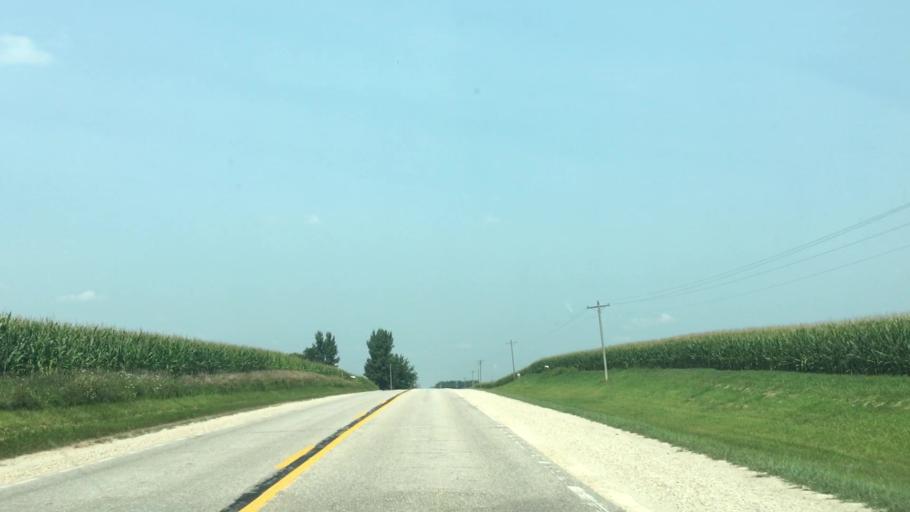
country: US
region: Iowa
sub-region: Buchanan County
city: Independence
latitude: 42.3656
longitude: -91.8893
